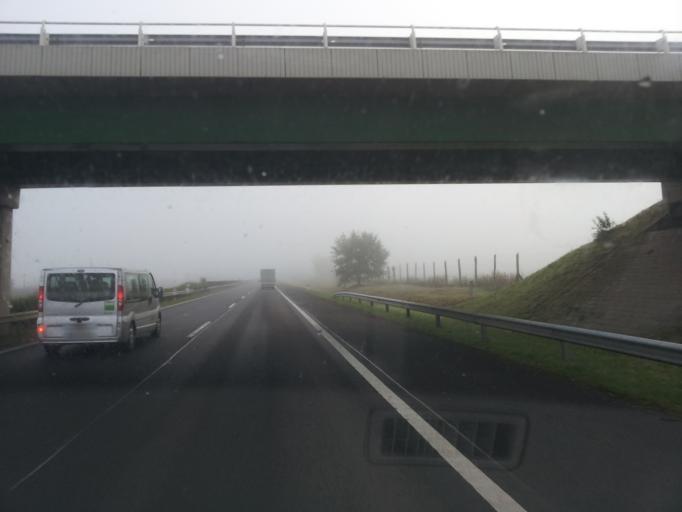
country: HU
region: Heves
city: Hatvan
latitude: 47.6784
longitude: 19.6521
